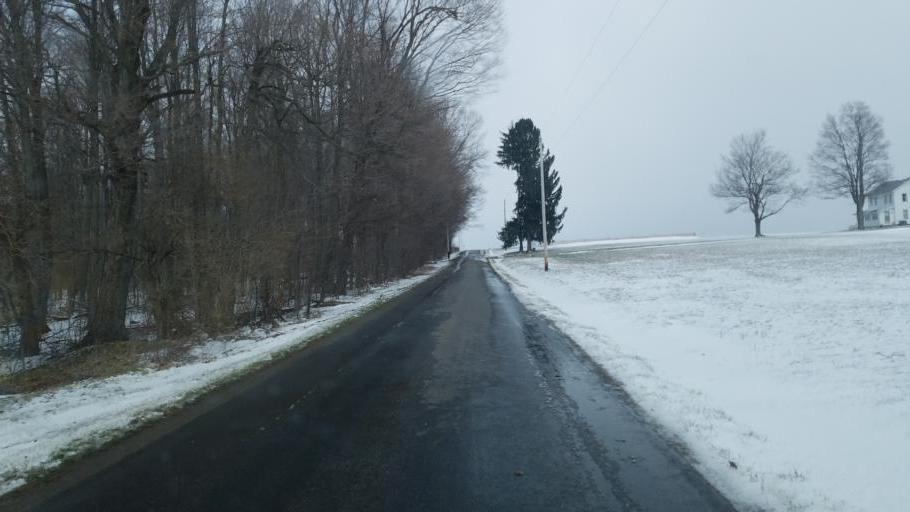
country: US
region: Ohio
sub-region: Richland County
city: Lexington
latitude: 40.5972
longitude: -82.6242
